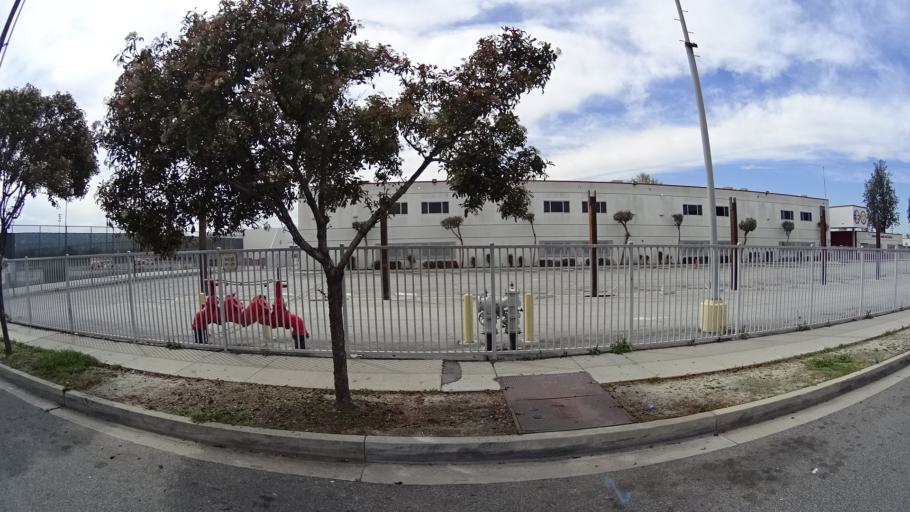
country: US
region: California
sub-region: Los Angeles County
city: Baldwin Park
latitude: 34.0767
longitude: -117.9784
